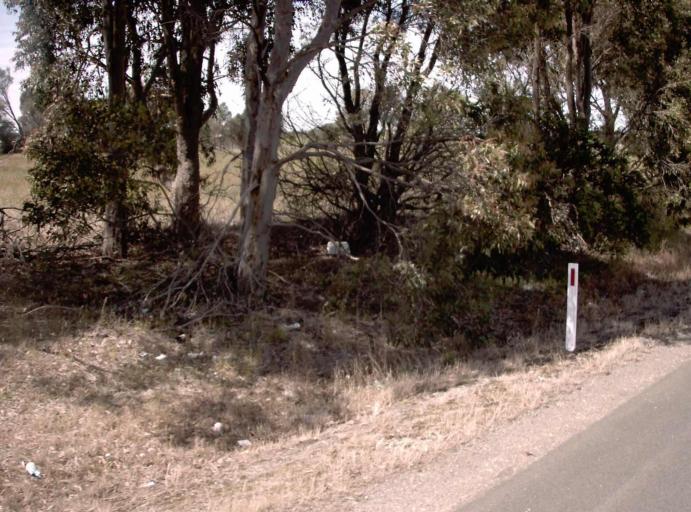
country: AU
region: Victoria
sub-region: Wellington
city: Sale
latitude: -38.1007
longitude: 146.9999
